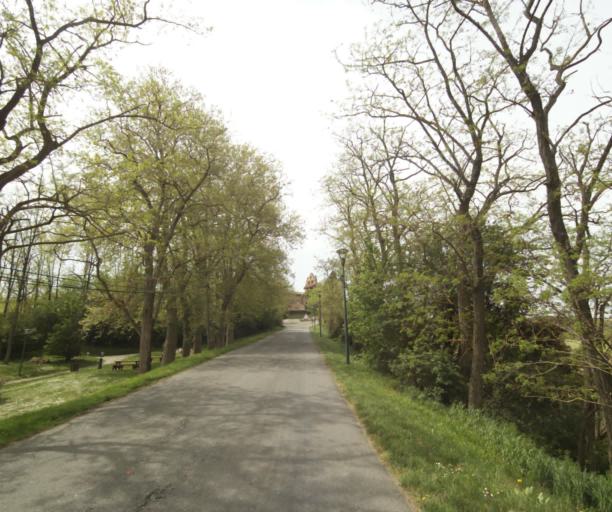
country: FR
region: Midi-Pyrenees
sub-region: Departement de la Haute-Garonne
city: Pompertuzat
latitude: 43.4889
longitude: 1.5138
